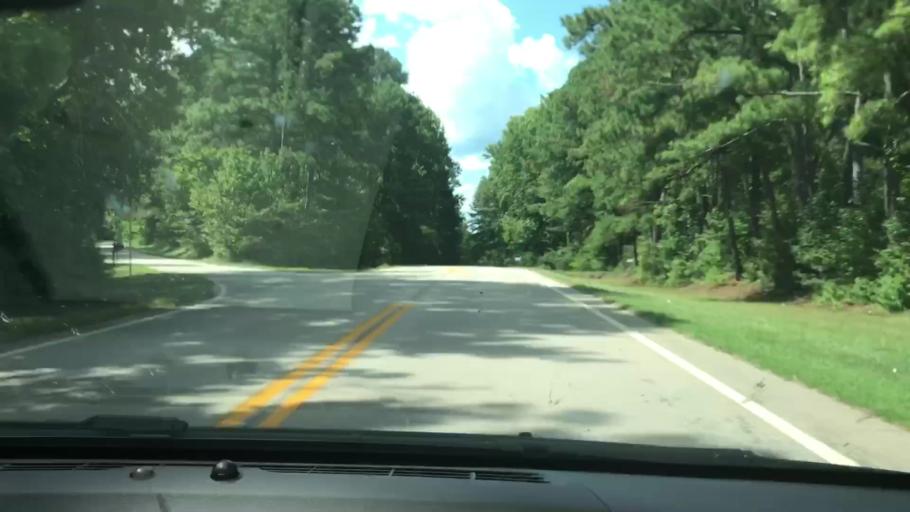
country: US
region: Georgia
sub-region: Troup County
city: La Grange
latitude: 33.1126
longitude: -85.0831
